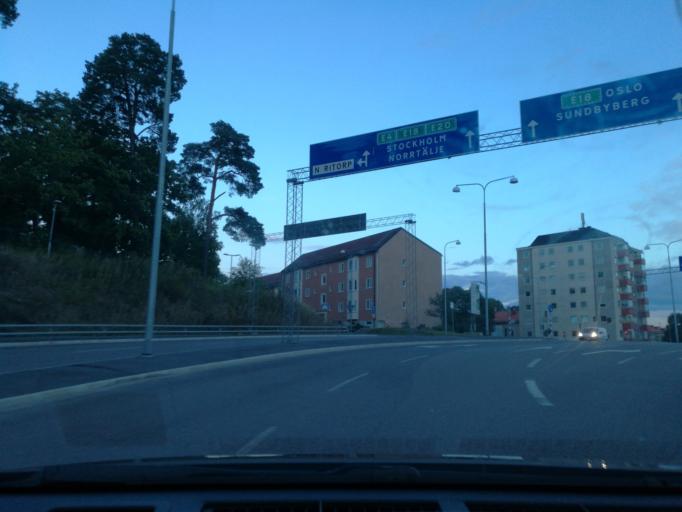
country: SE
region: Stockholm
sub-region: Solna Kommun
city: Solna
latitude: 59.3776
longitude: 18.0039
